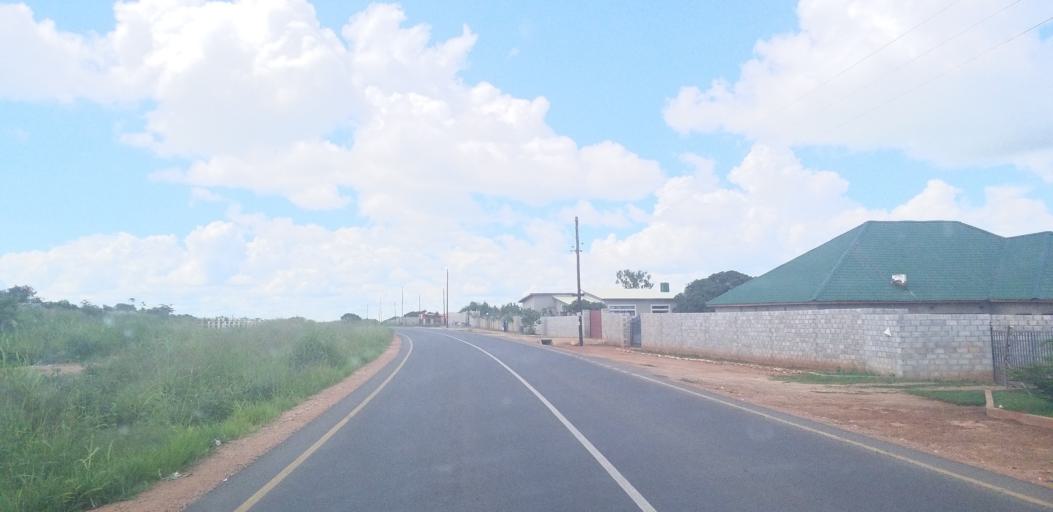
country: ZM
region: Lusaka
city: Lusaka
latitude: -15.3286
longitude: 28.3285
